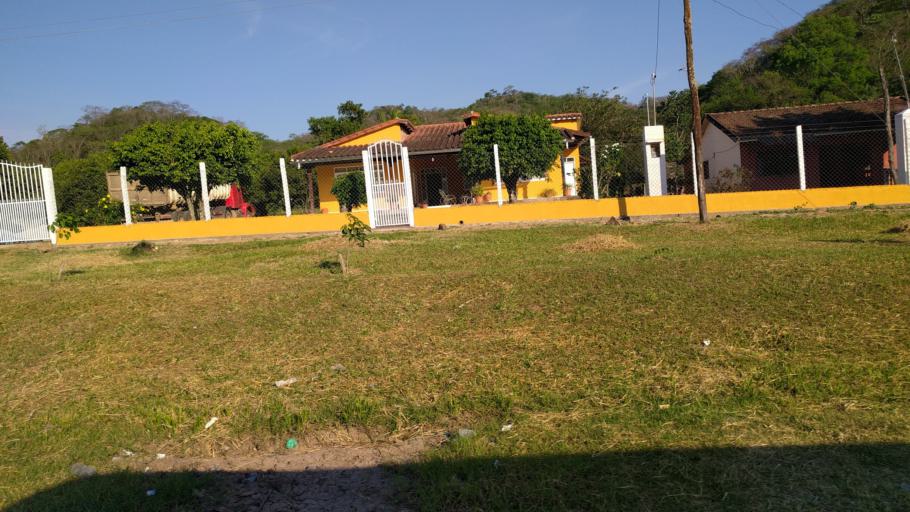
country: BO
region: Santa Cruz
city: Jorochito
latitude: -18.0694
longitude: -63.4396
